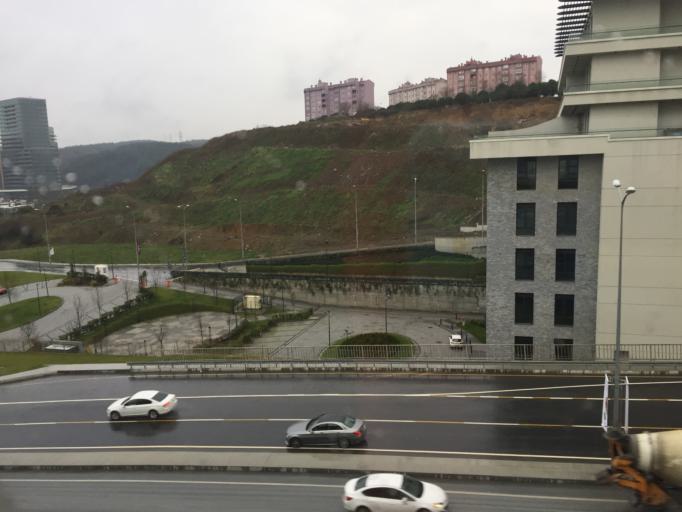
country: TR
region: Istanbul
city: Sisli
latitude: 41.1050
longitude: 28.9913
